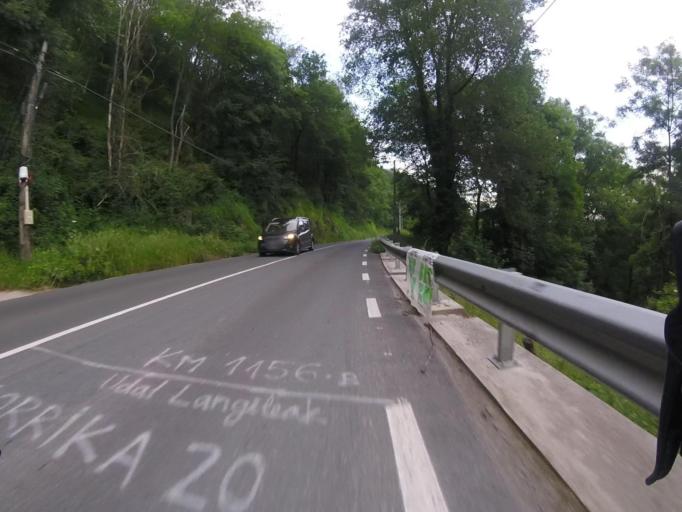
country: ES
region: Basque Country
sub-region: Provincia de Guipuzcoa
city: Errenteria
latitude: 43.2844
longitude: -1.9140
